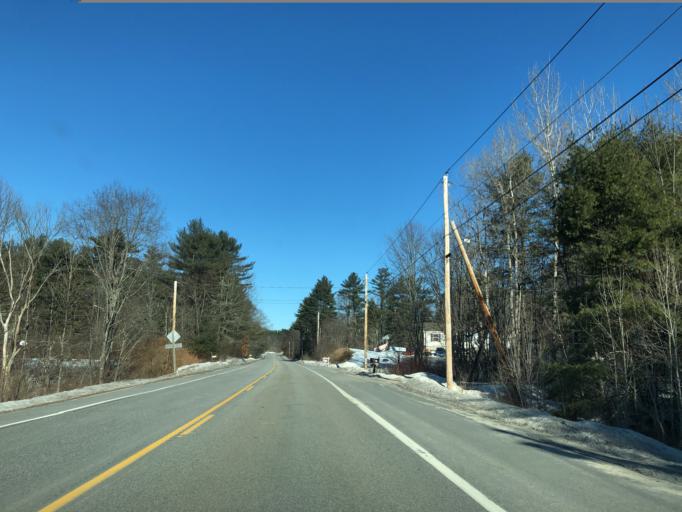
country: US
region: Maine
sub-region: Cumberland County
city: North Windham
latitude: 43.8340
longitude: -70.3820
